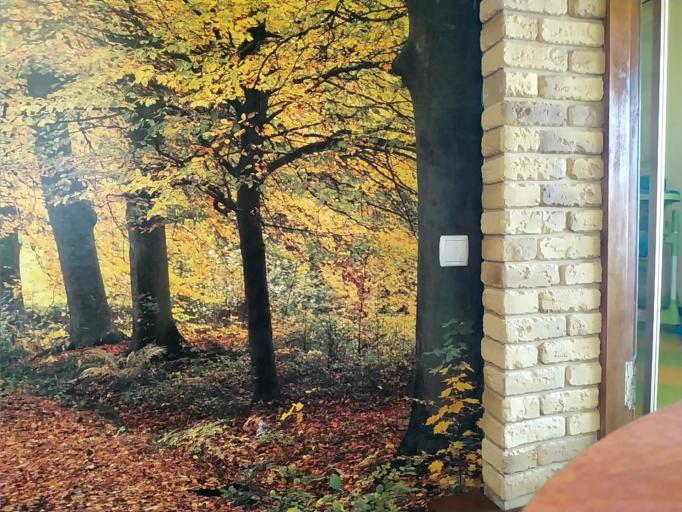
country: RU
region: Tverskaya
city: Maksatikha
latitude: 57.6099
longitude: 35.8270
